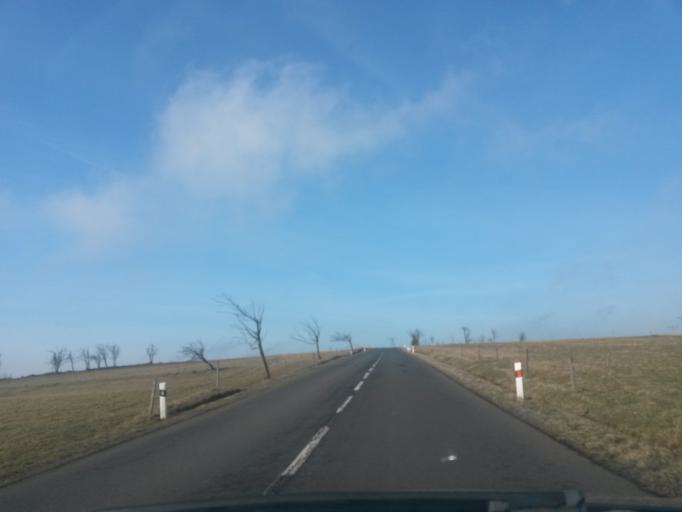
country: CZ
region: Ustecky
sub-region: Okres Chomutov
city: Perstejn
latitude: 50.4233
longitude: 13.1270
